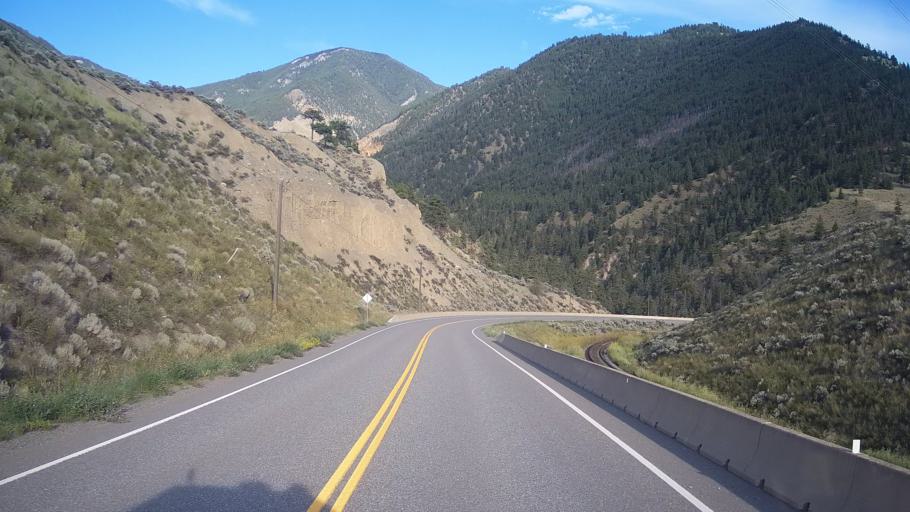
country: CA
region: British Columbia
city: Lillooet
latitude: 50.7951
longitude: -121.8402
